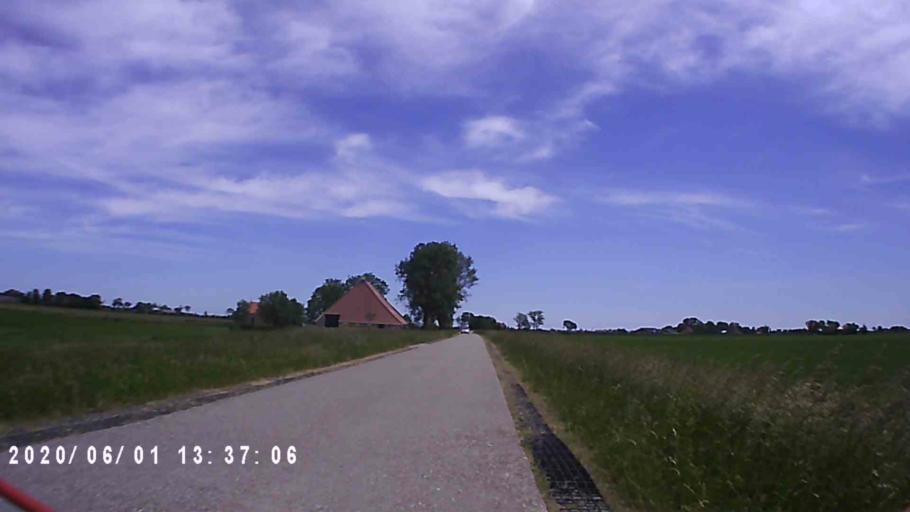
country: NL
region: Friesland
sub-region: Gemeente Littenseradiel
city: Wommels
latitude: 53.0861
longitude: 5.5922
